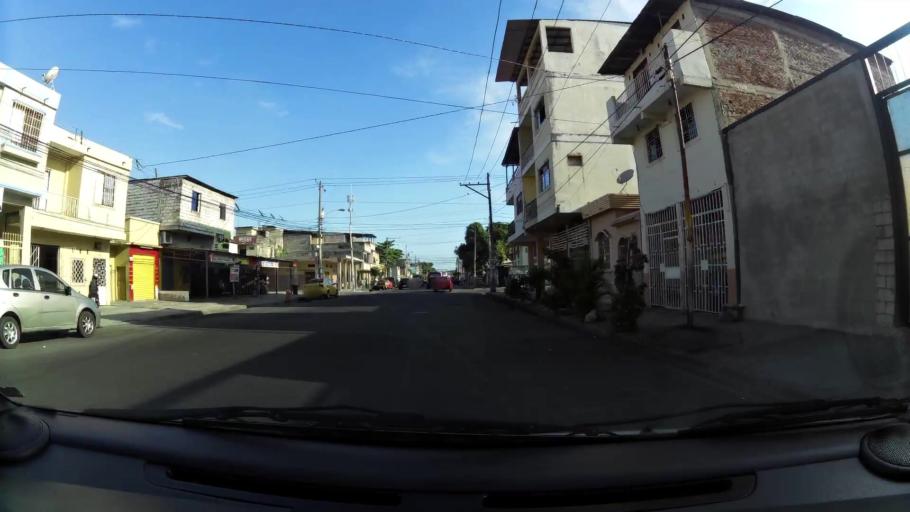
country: EC
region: Guayas
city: Guayaquil
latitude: -2.2159
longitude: -79.9027
